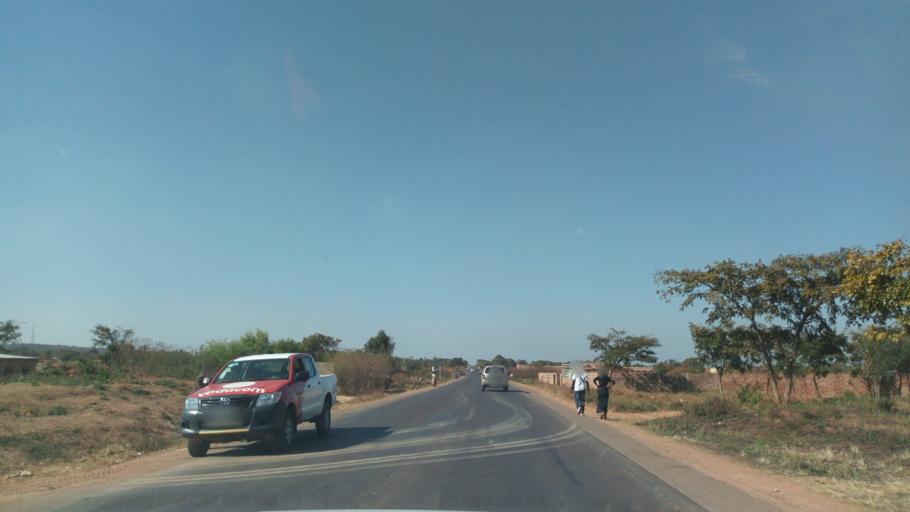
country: CD
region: Katanga
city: Lubumbashi
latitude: -11.5552
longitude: 27.5820
